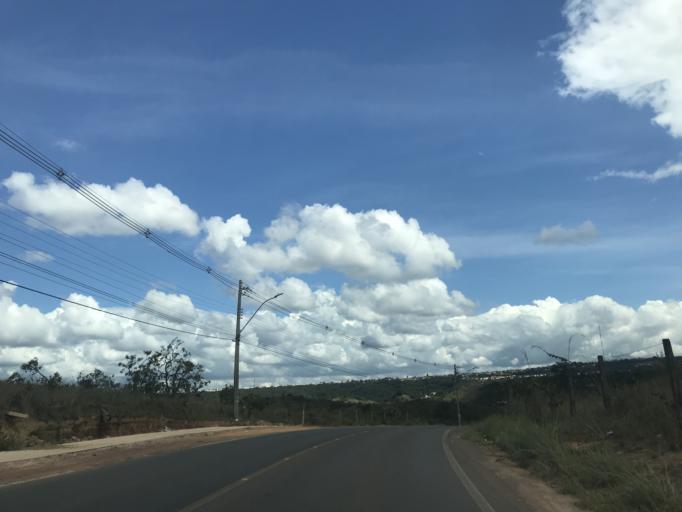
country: BR
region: Federal District
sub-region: Brasilia
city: Brasilia
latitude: -15.8678
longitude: -47.7783
